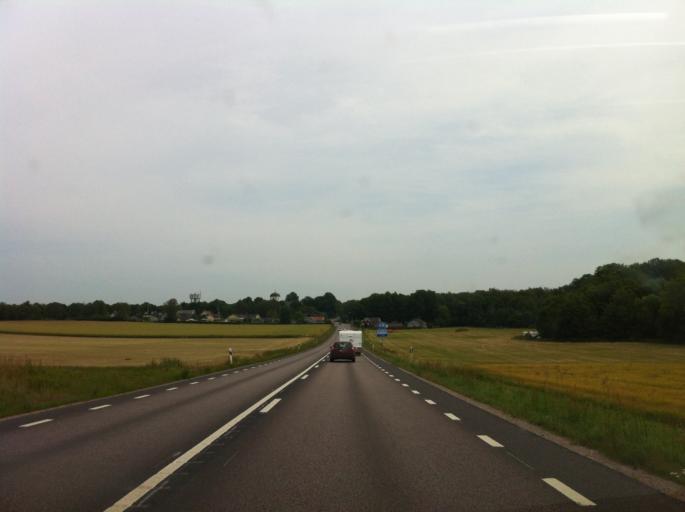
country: SE
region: Blekinge
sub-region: Karlskrona Kommun
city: Jaemjoe
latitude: 56.1880
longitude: 15.8176
